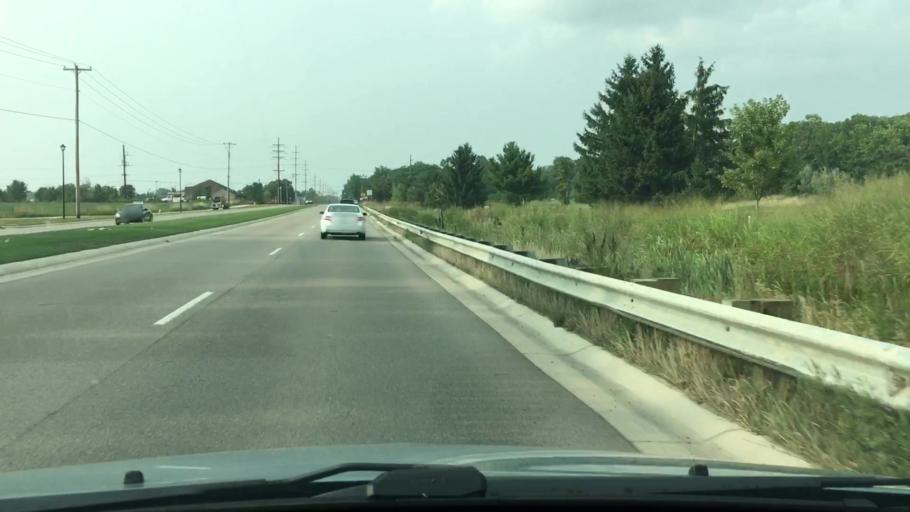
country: US
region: Michigan
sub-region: Ottawa County
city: Allendale
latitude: 42.9688
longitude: -85.9042
